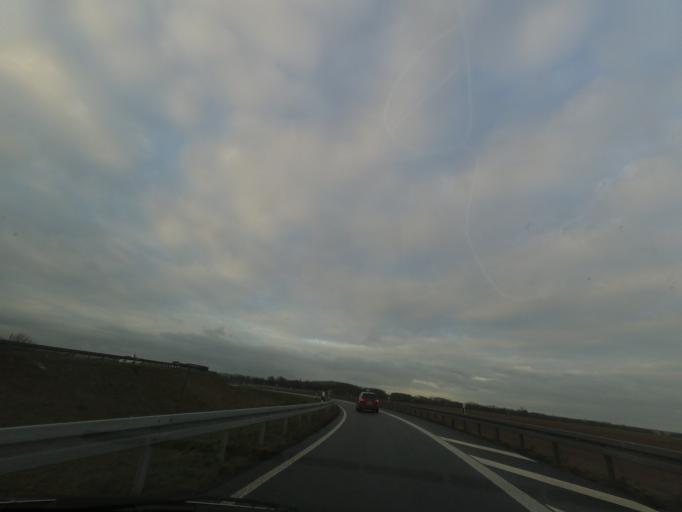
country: DE
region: North Rhine-Westphalia
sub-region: Regierungsbezirk Koln
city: Titz
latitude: 51.0352
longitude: 6.4720
